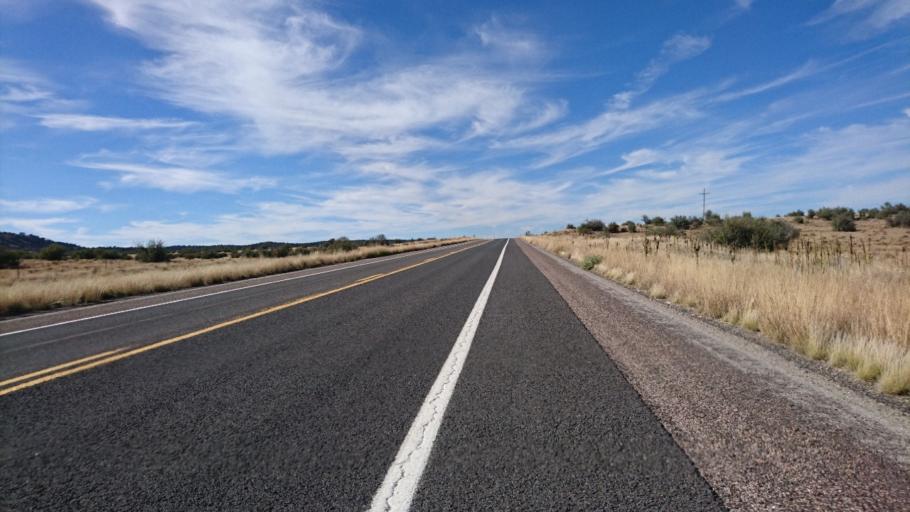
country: US
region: Arizona
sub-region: Mohave County
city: Peach Springs
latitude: 35.4930
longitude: -113.1607
